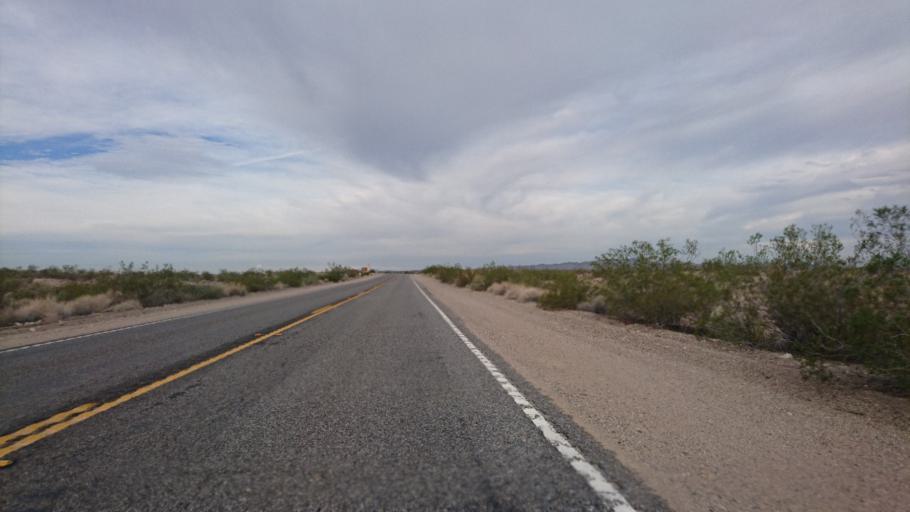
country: US
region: Arizona
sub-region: Mohave County
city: Willow Valley
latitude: 34.9350
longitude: -114.8033
